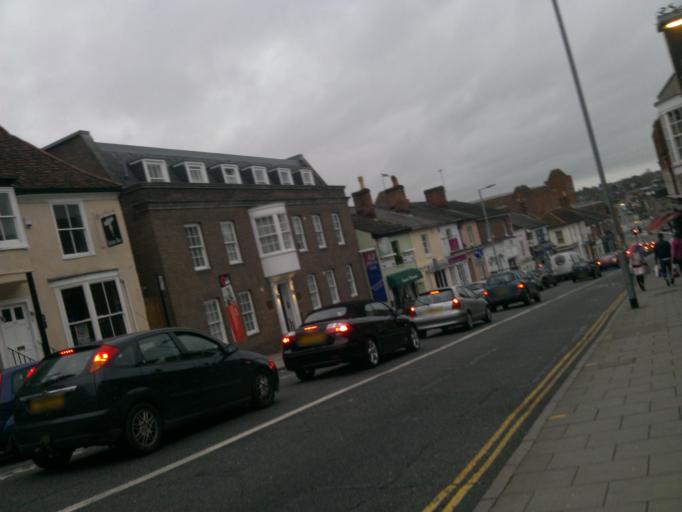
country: GB
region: England
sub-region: Essex
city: Colchester
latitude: 51.8911
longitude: 0.8961
